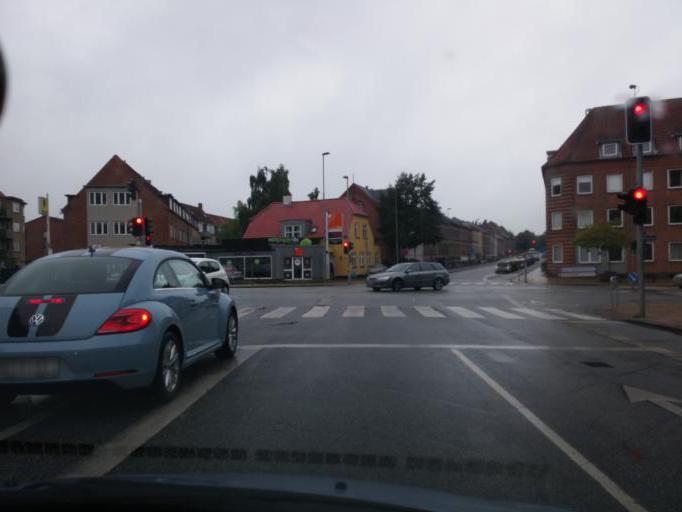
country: DK
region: South Denmark
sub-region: Odense Kommune
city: Odense
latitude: 55.3945
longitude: 10.4053
